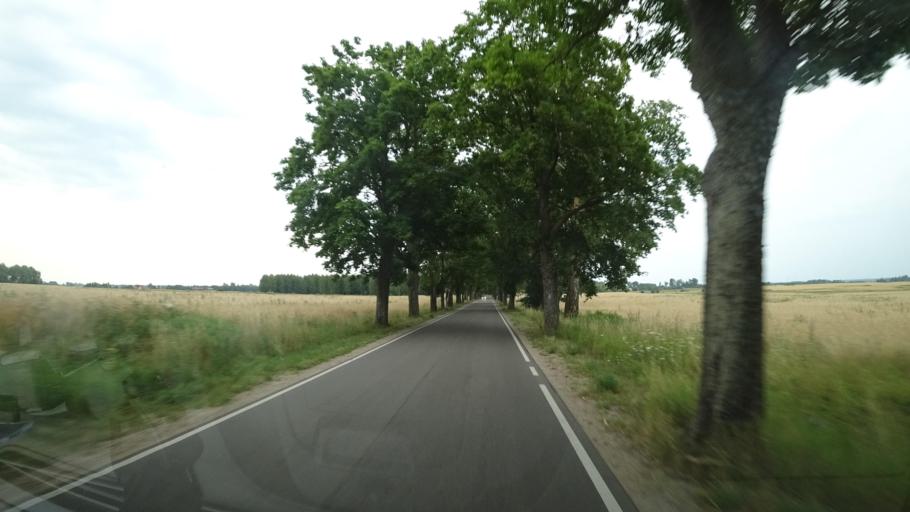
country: PL
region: Warmian-Masurian Voivodeship
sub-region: Powiat mragowski
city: Mikolajki
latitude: 53.8577
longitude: 21.6094
